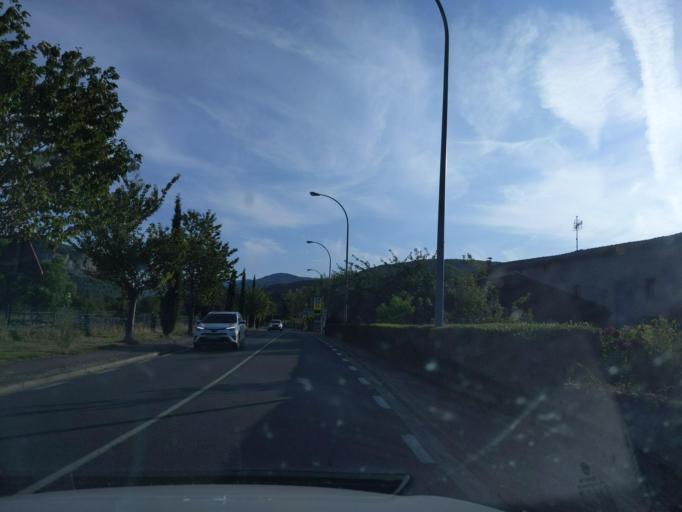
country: ES
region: La Rioja
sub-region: Provincia de La Rioja
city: Ojacastro
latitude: 42.3507
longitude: -2.9990
